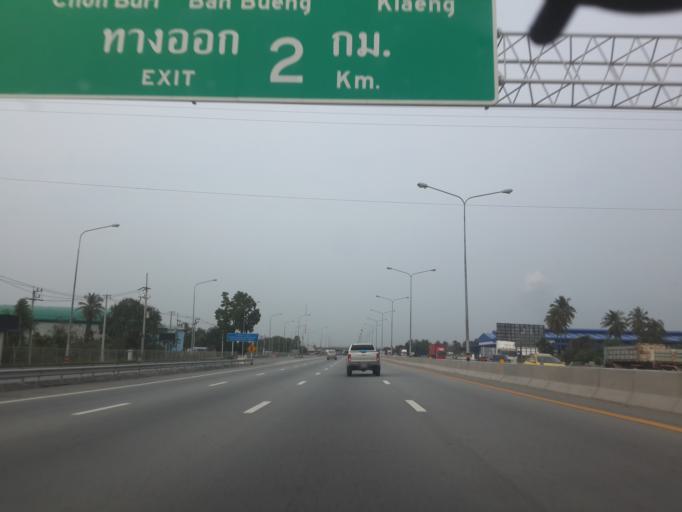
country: TH
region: Chon Buri
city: Chon Buri
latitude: 13.3188
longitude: 101.0105
